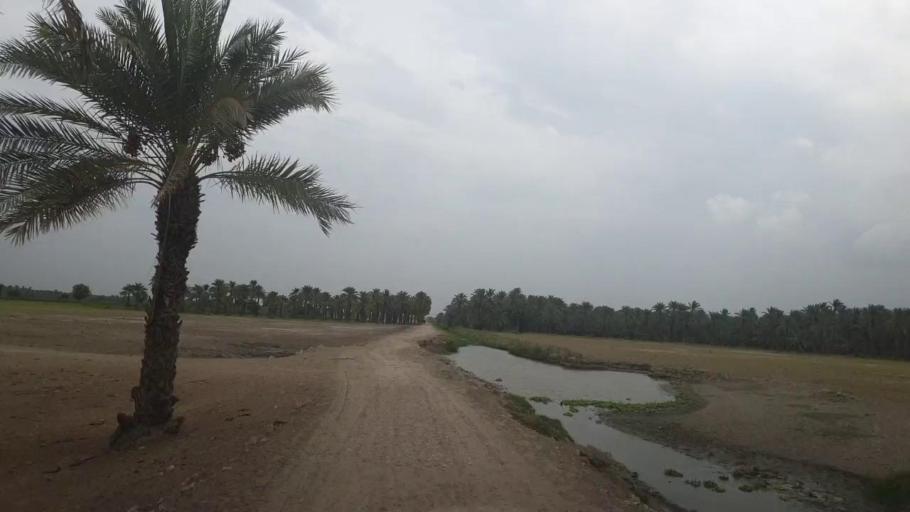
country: PK
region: Sindh
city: Khairpur
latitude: 27.5599
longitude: 68.7091
